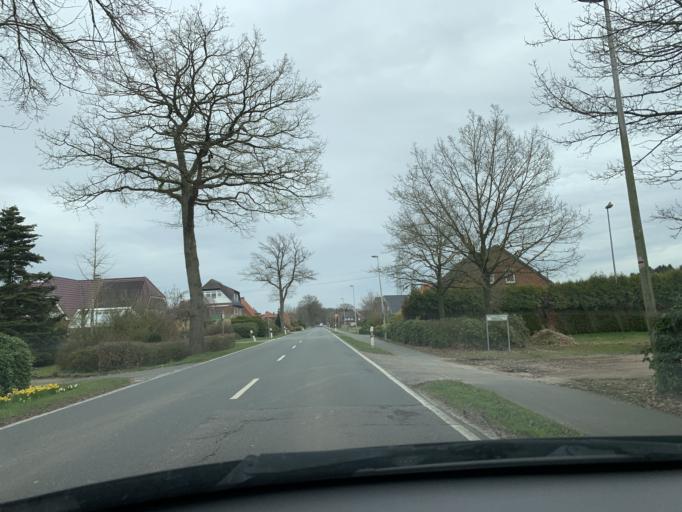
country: DE
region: Lower Saxony
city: Bad Zwischenahn
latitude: 53.1760
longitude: 7.9710
